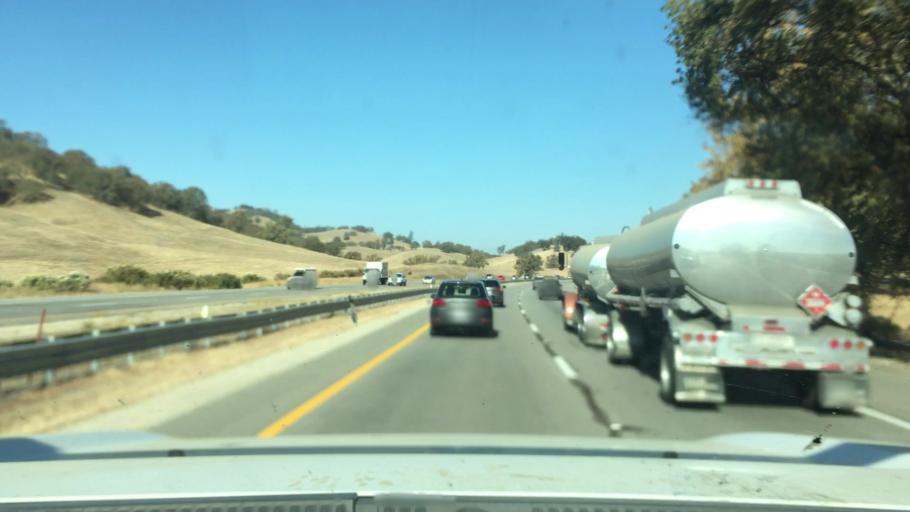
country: US
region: California
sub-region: San Luis Obispo County
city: Santa Margarita
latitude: 35.4060
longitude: -120.6248
